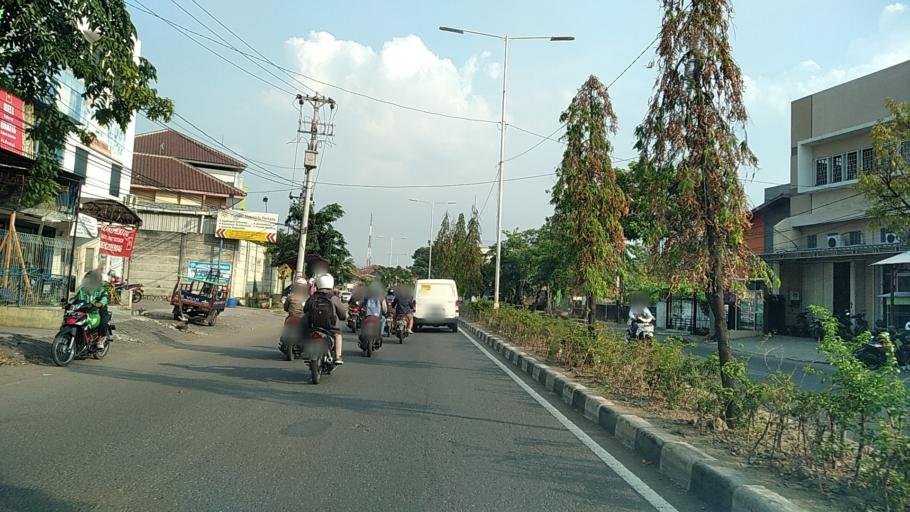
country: ID
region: Central Java
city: Semarang
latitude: -6.9921
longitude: 110.4589
